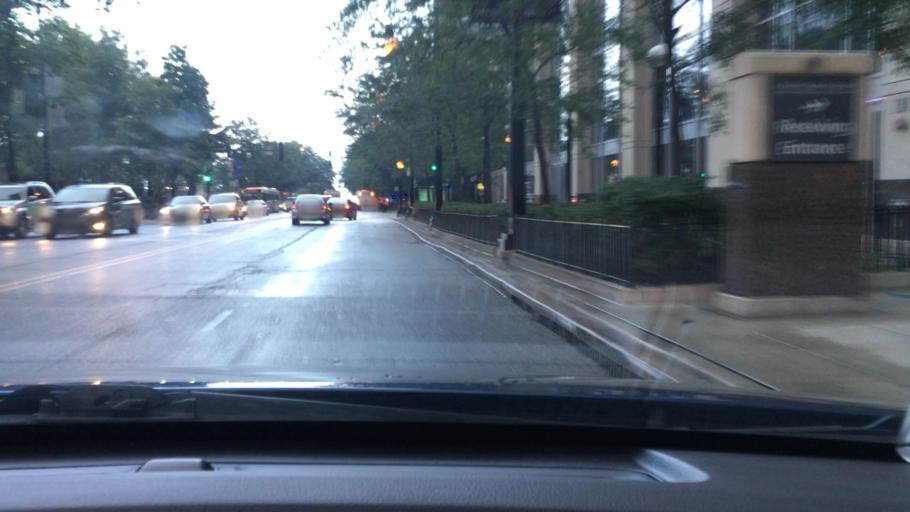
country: US
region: Illinois
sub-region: Cook County
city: Chicago
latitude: 41.8967
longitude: -87.6215
